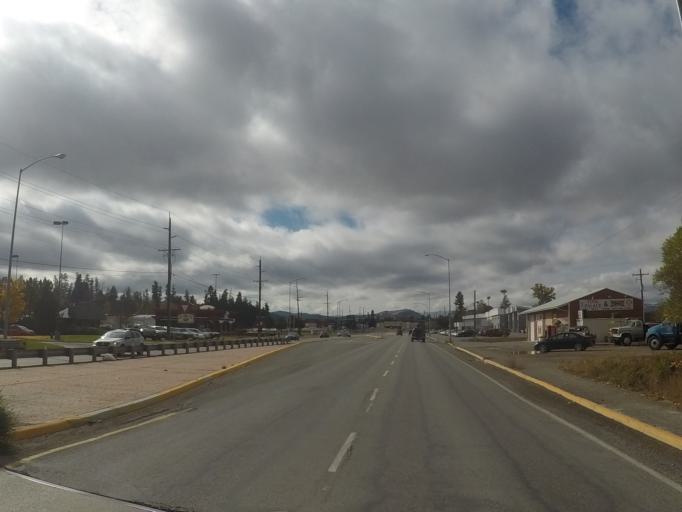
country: US
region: Montana
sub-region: Flathead County
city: Evergreen
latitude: 48.2116
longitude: -114.2854
